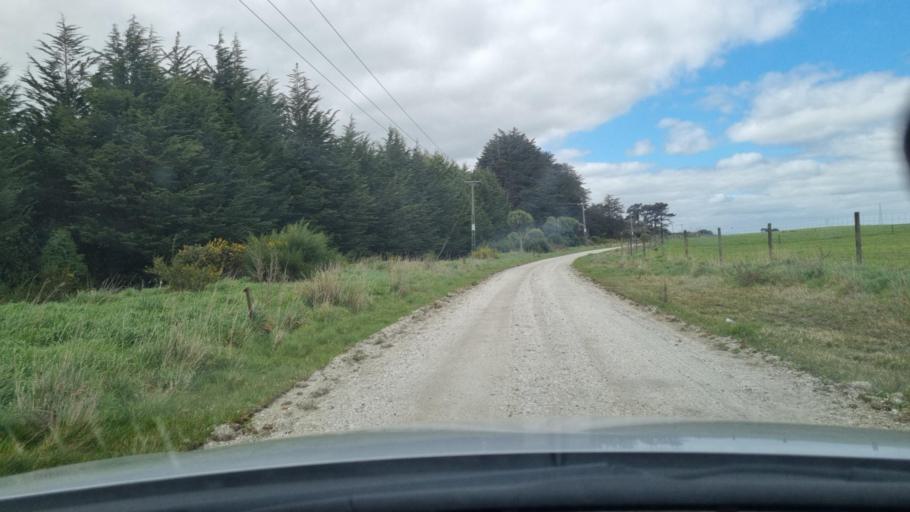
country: NZ
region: Southland
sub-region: Invercargill City
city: Invercargill
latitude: -46.4429
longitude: 168.4226
